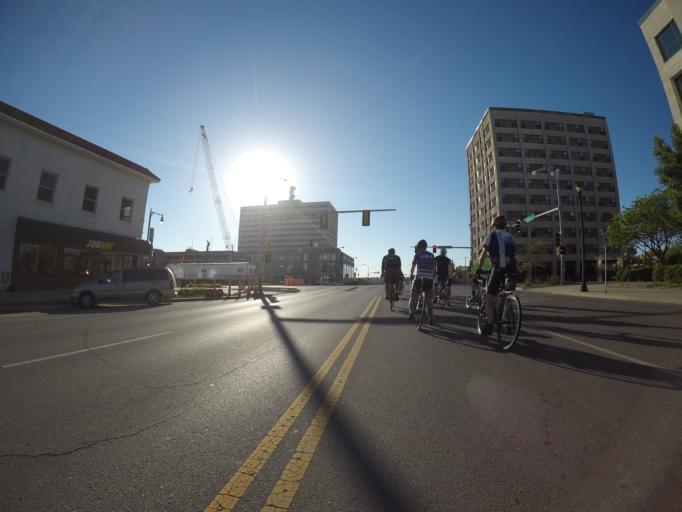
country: US
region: Kansas
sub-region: Shawnee County
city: Topeka
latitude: 39.0460
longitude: -95.6762
